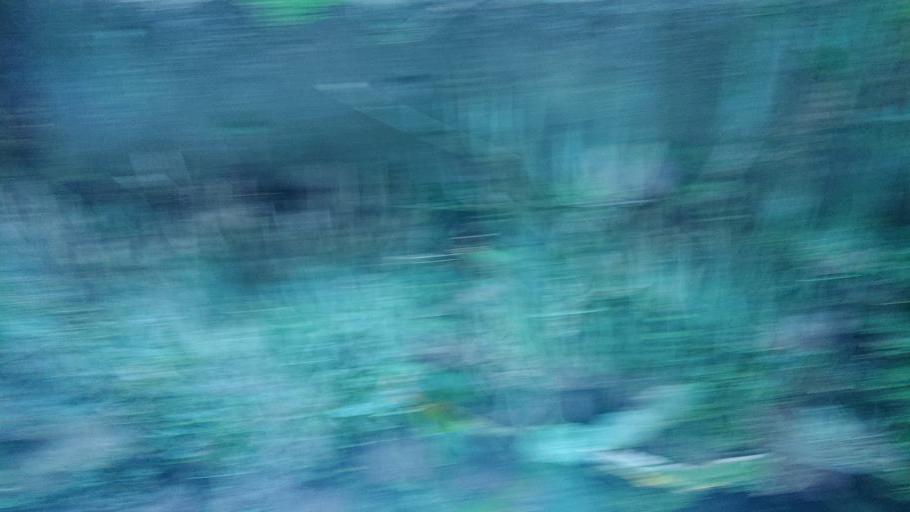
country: TW
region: Taiwan
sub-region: Yunlin
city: Douliu
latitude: 23.5298
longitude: 120.6599
